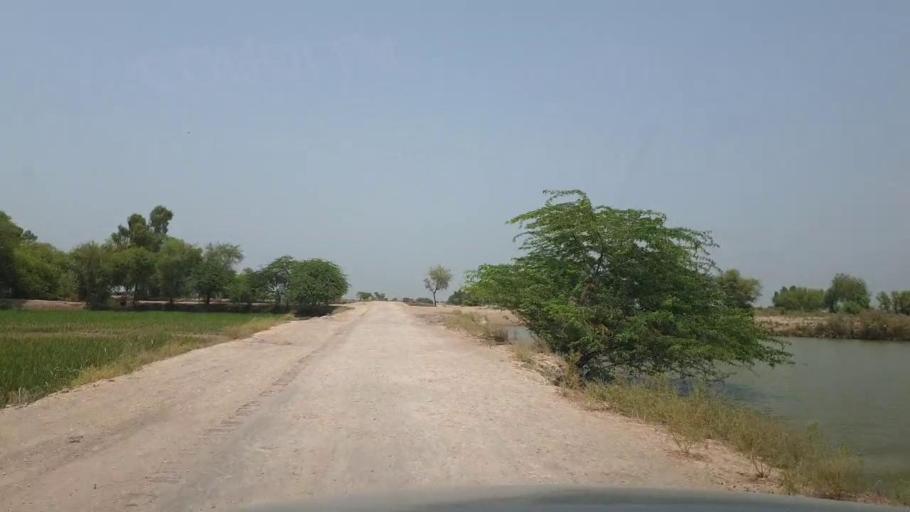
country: PK
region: Sindh
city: Garhi Yasin
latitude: 27.8779
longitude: 68.4454
